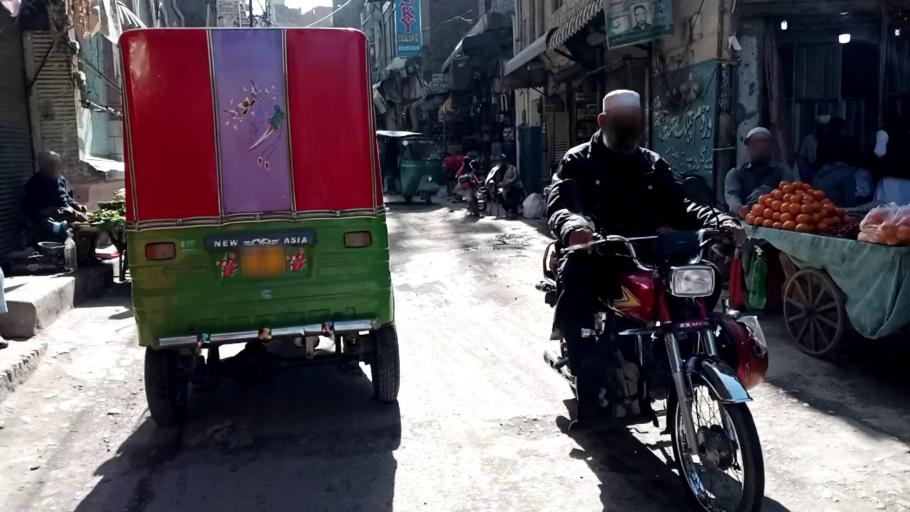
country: PK
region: Khyber Pakhtunkhwa
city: Peshawar
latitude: 34.0126
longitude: 71.5806
